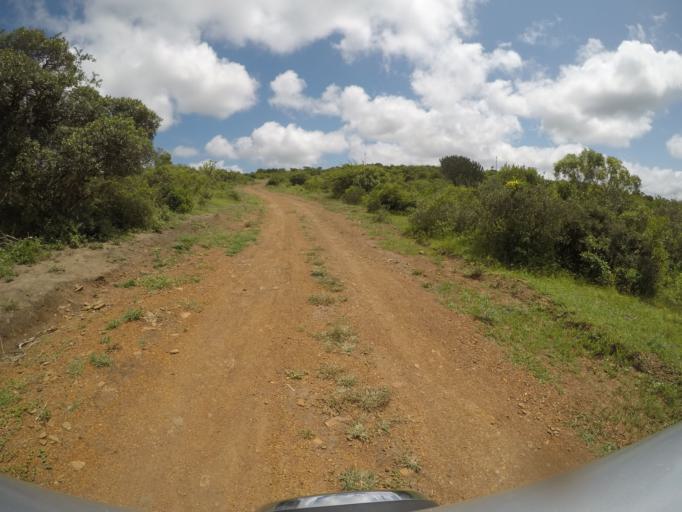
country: ZA
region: KwaZulu-Natal
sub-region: uThungulu District Municipality
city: Empangeni
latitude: -28.5852
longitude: 31.8281
